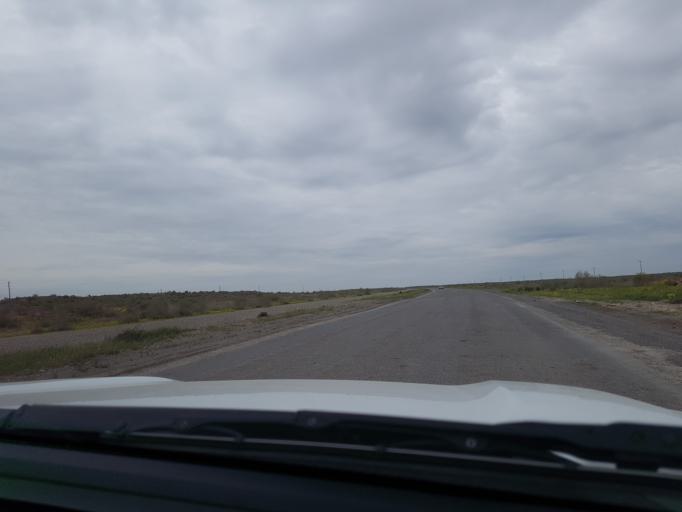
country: TM
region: Mary
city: Bayramaly
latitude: 37.9346
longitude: 62.6279
